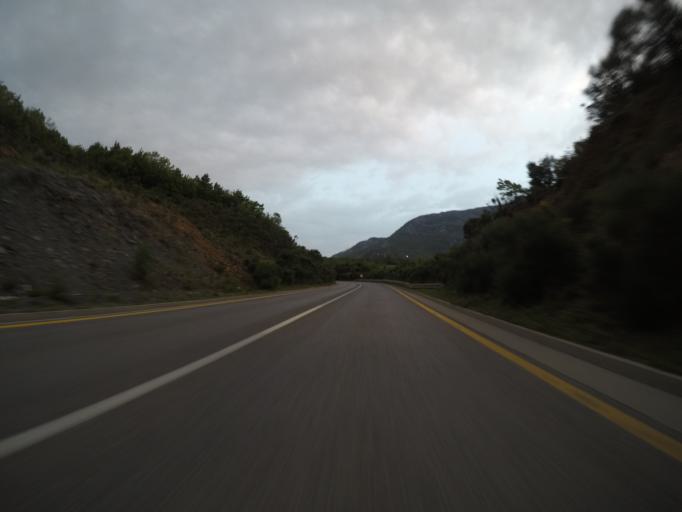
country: ME
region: Bar
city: Sutomore
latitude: 42.1548
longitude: 19.0283
